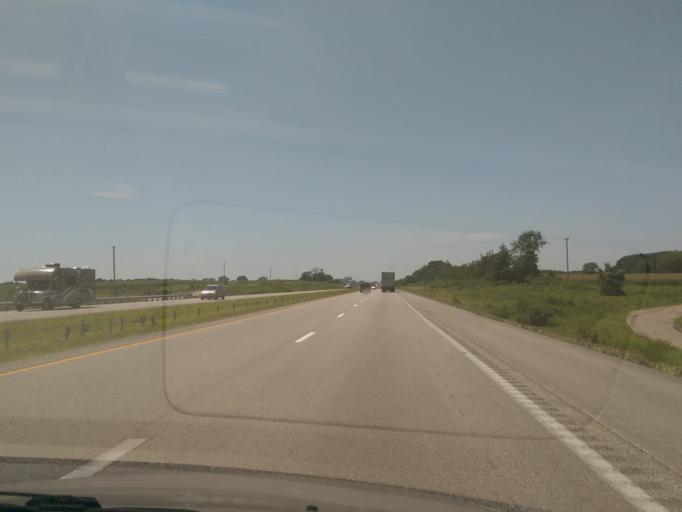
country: US
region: Missouri
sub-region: Saline County
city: Sweet Springs
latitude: 38.9722
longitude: -93.2884
